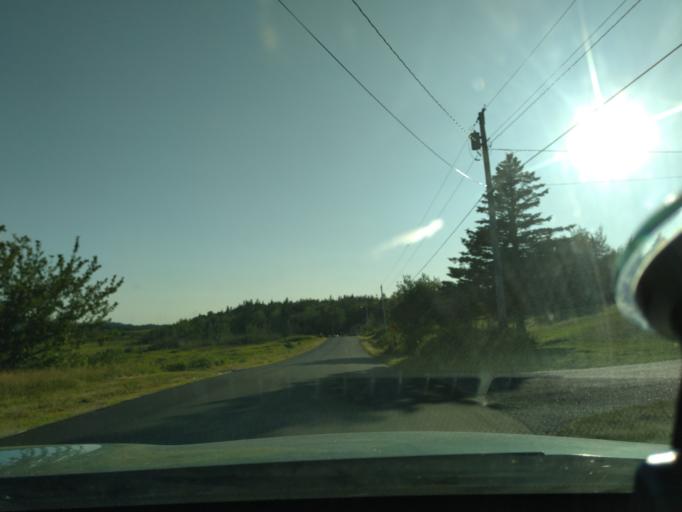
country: US
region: Maine
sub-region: Washington County
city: Machiasport
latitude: 44.6821
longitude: -67.1842
